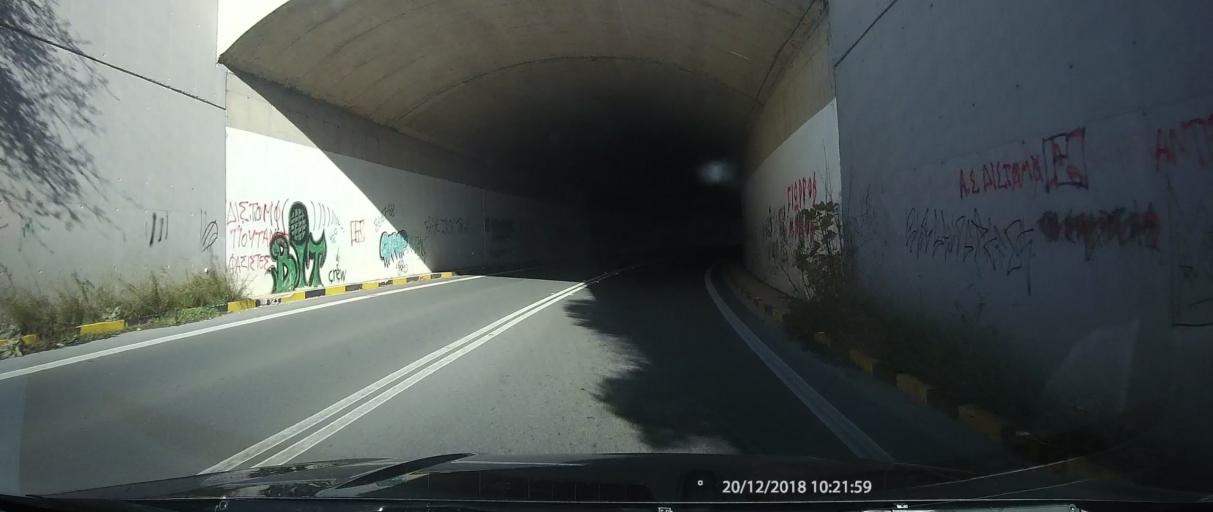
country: GR
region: Peloponnese
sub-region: Nomos Lakonias
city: Magoula
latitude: 37.1682
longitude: 22.4254
